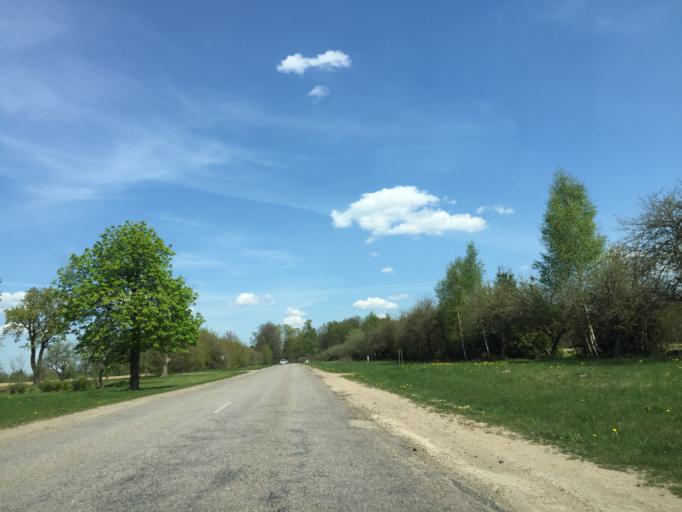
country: LV
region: Krimulda
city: Ragana
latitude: 57.3300
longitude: 24.6424
